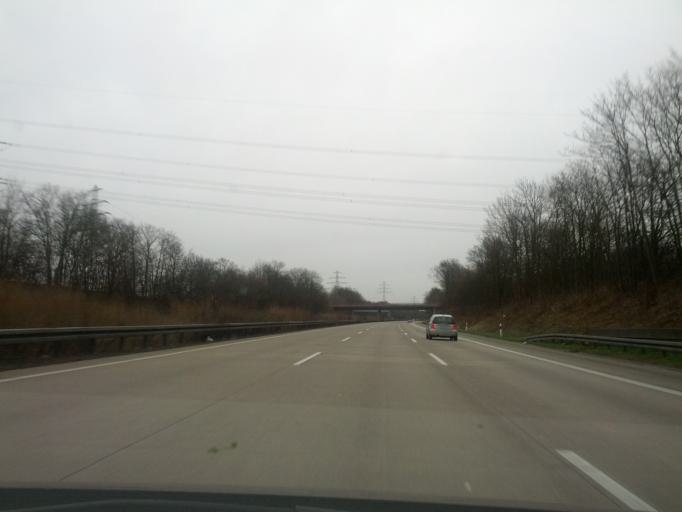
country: DE
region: Lower Saxony
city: Algermissen
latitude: 52.2764
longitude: 9.9110
